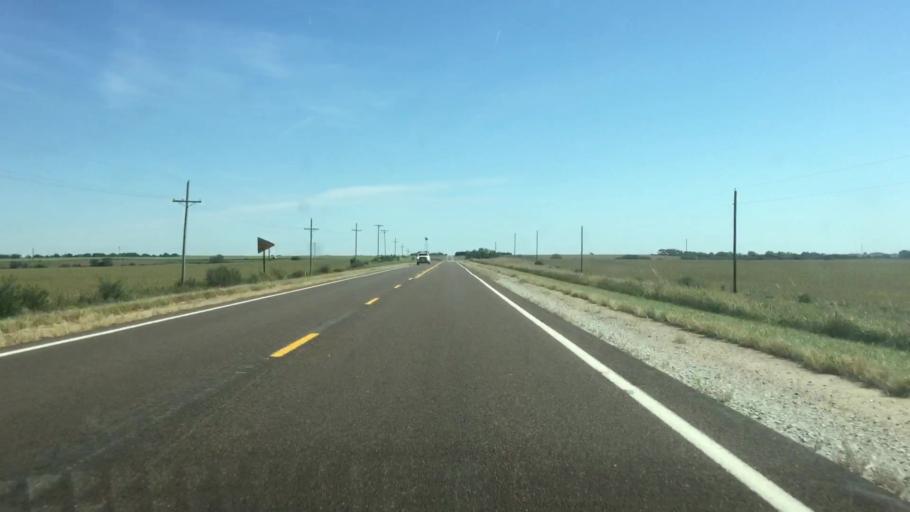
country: US
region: Nebraska
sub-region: Jefferson County
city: Fairbury
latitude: 40.1472
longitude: -97.3355
